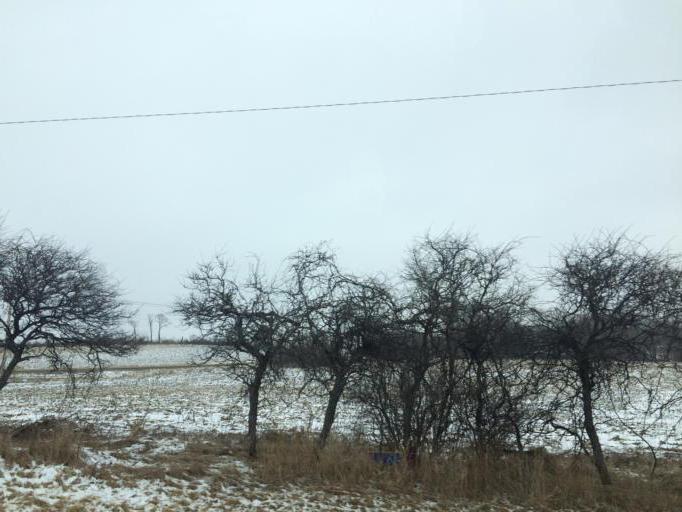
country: US
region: Illinois
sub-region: McHenry County
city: Woodstock
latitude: 42.2702
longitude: -88.4330
